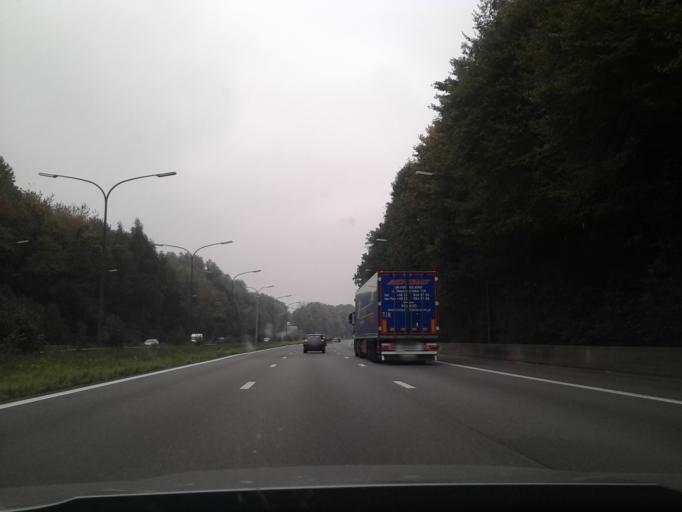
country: BE
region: Flanders
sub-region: Provincie Vlaams-Brabant
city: Halle
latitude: 50.7366
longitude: 4.2720
